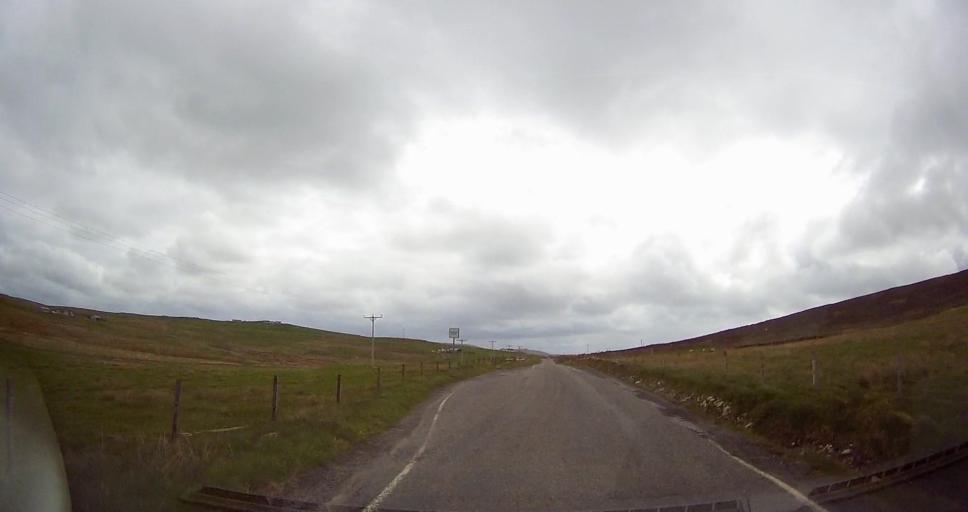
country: GB
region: Scotland
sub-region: Shetland Islands
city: Sandwick
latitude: 60.2483
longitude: -1.5096
